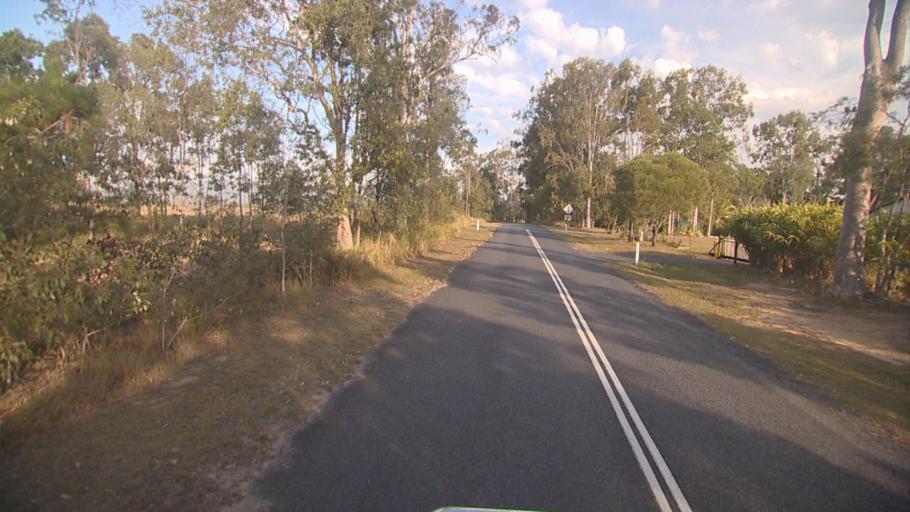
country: AU
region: Queensland
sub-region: Logan
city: Chambers Flat
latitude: -27.8399
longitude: 153.1189
